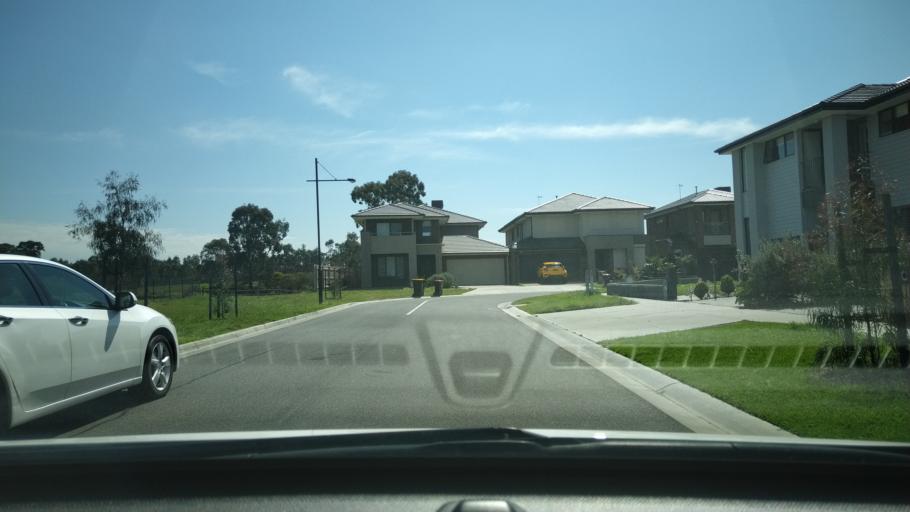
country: AU
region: Victoria
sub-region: Greater Dandenong
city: Keysborough
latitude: -38.0015
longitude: 145.1774
